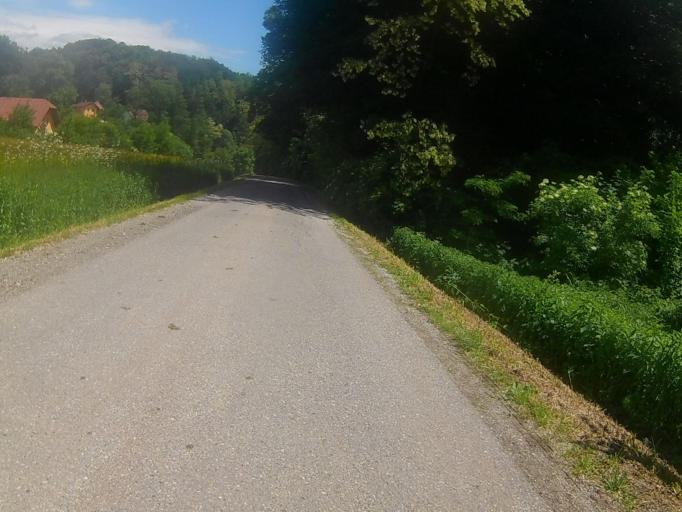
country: SI
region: Duplek
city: Zgornji Duplek
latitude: 46.5420
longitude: 15.7292
